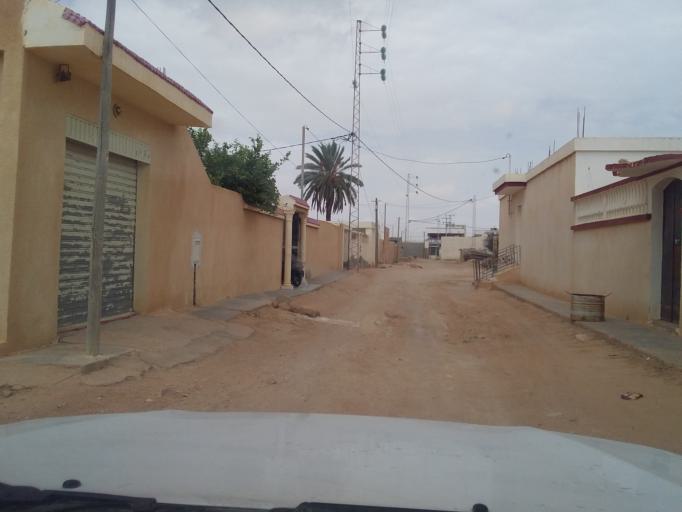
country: TN
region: Qabis
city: Matmata
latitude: 33.6187
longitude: 10.2648
